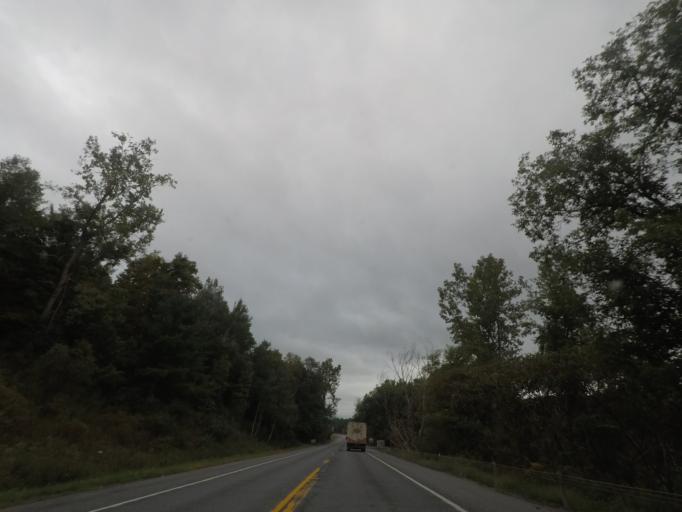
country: US
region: New York
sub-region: Rensselaer County
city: Hoosick Falls
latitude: 42.9397
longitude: -73.3657
